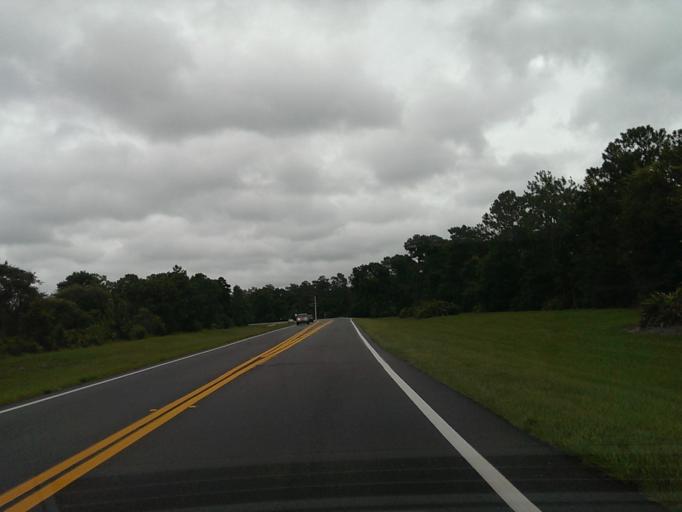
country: US
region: Florida
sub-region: Osceola County
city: Celebration
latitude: 28.3907
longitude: -81.5358
